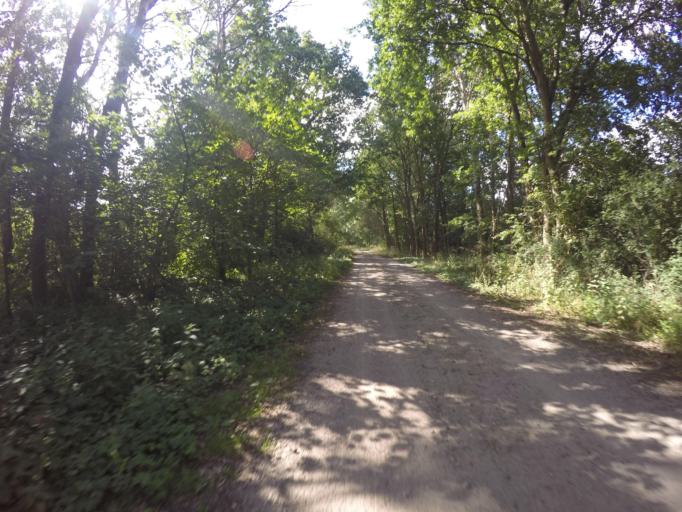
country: DE
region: Lower Saxony
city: Thomasburg
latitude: 53.2605
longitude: 10.6538
